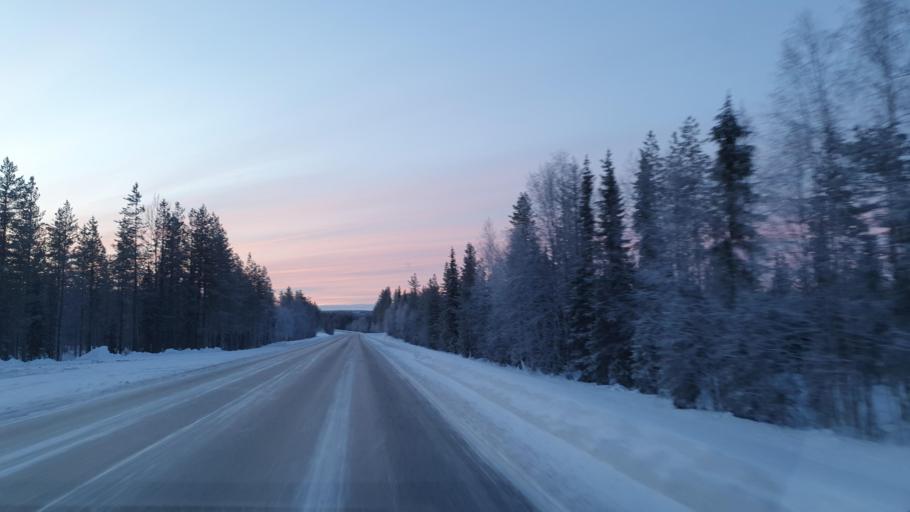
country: FI
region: Lapland
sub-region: Torniolaakso
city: Pello
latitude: 67.0316
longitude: 24.0359
